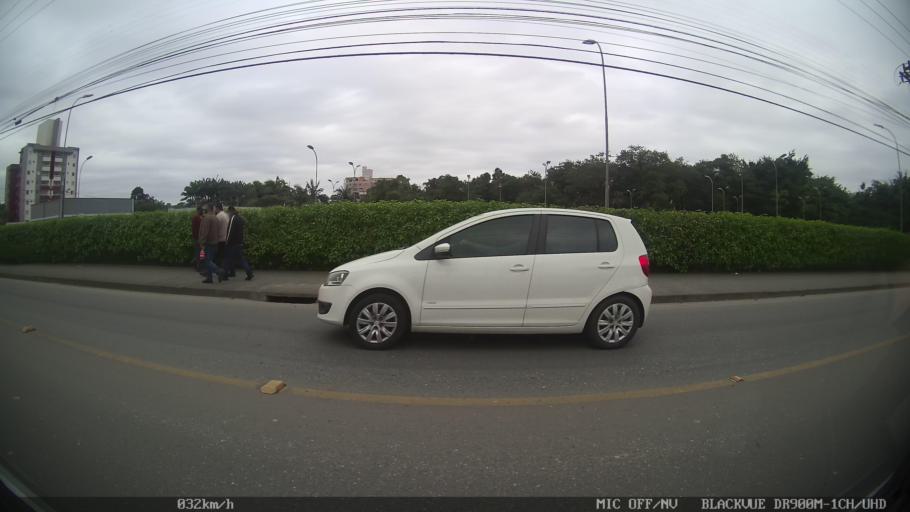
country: BR
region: Santa Catarina
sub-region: Joinville
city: Joinville
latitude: -26.2647
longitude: -48.8696
